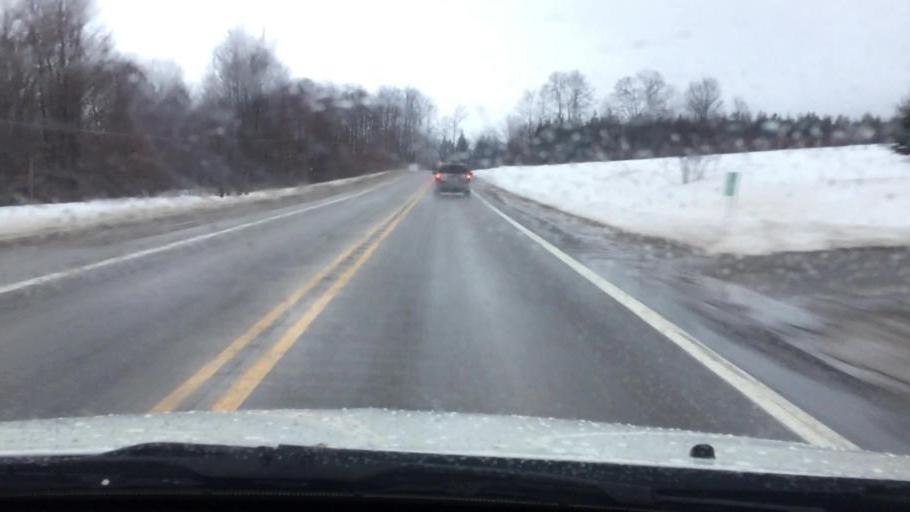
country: US
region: Michigan
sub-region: Charlevoix County
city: East Jordan
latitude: 45.1956
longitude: -85.1648
